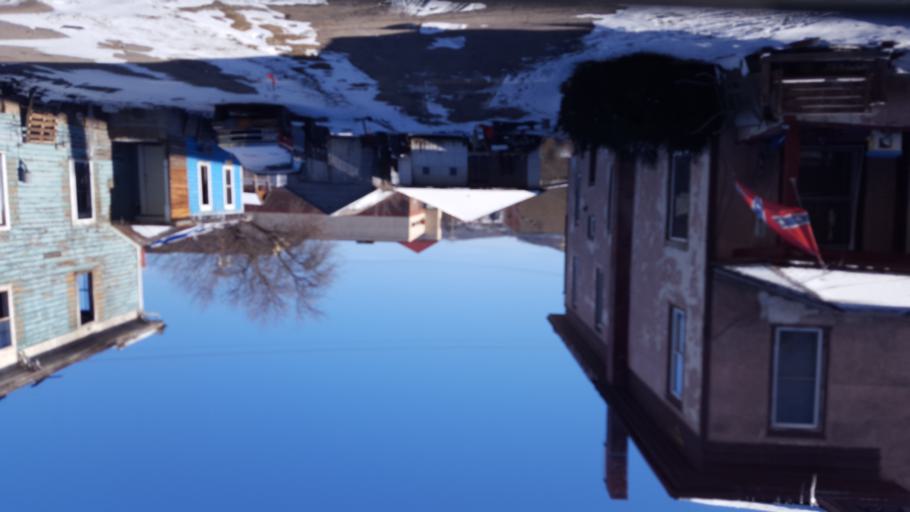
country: US
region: New York
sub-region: Allegany County
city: Wellsville
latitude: 42.1207
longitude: -77.9437
